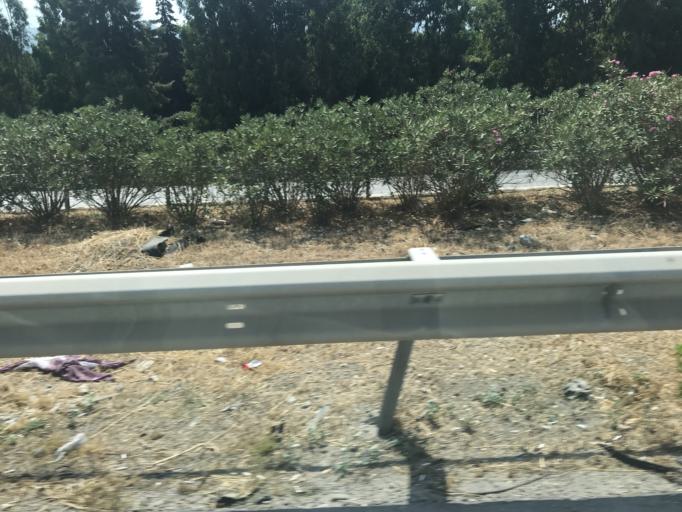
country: TR
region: Izmir
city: Karsiyaka
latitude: 38.3910
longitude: 26.9558
